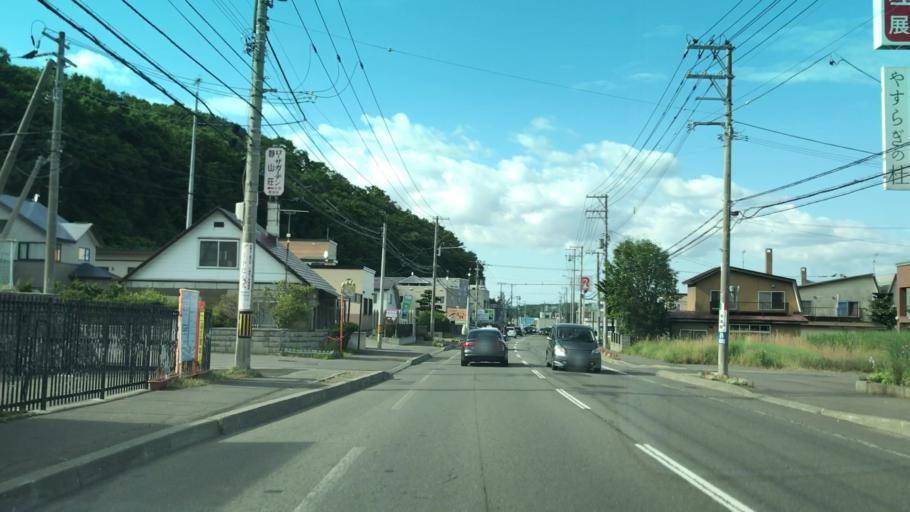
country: JP
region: Hokkaido
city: Sapporo
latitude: 42.9610
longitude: 141.3433
